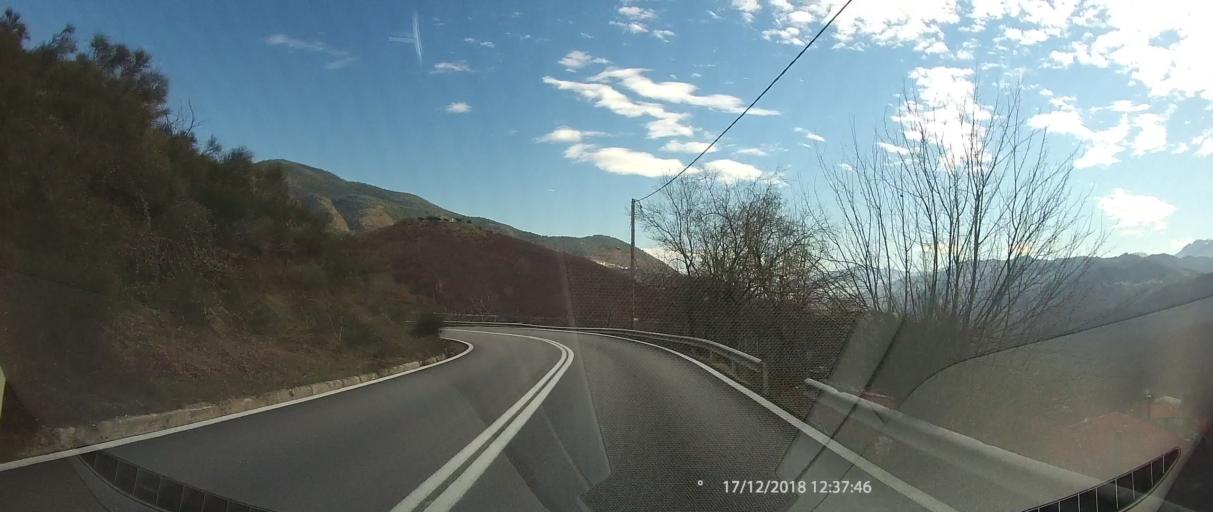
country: GR
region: Epirus
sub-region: Nomos Ioanninon
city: Metsovo
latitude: 39.8089
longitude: 21.3400
